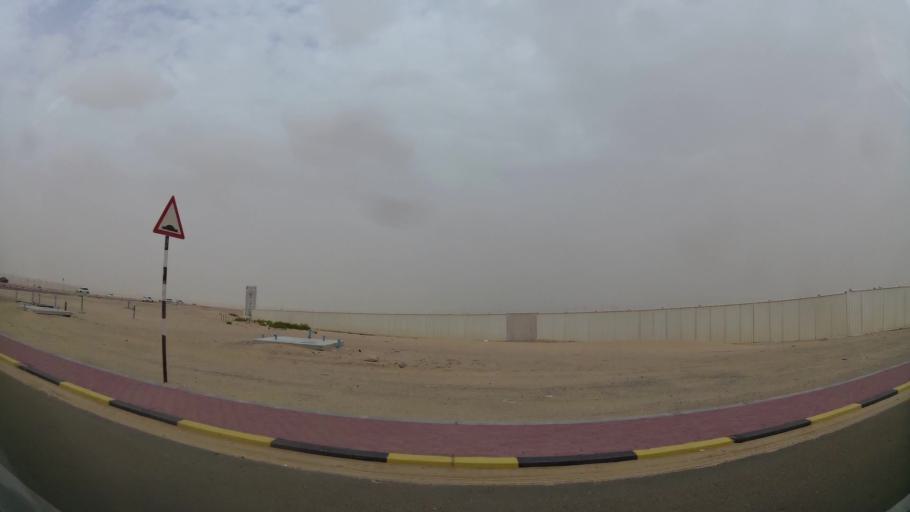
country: AE
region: Abu Dhabi
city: Abu Dhabi
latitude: 24.4260
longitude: 54.7133
